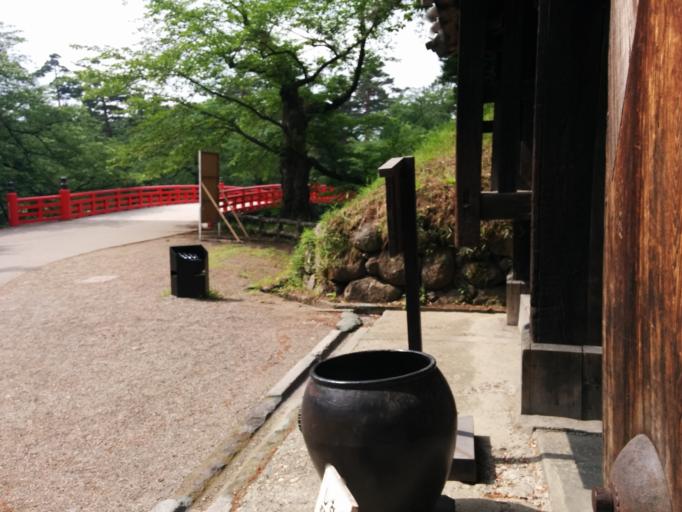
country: JP
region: Aomori
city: Hirosaki
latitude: 40.6062
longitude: 140.4636
